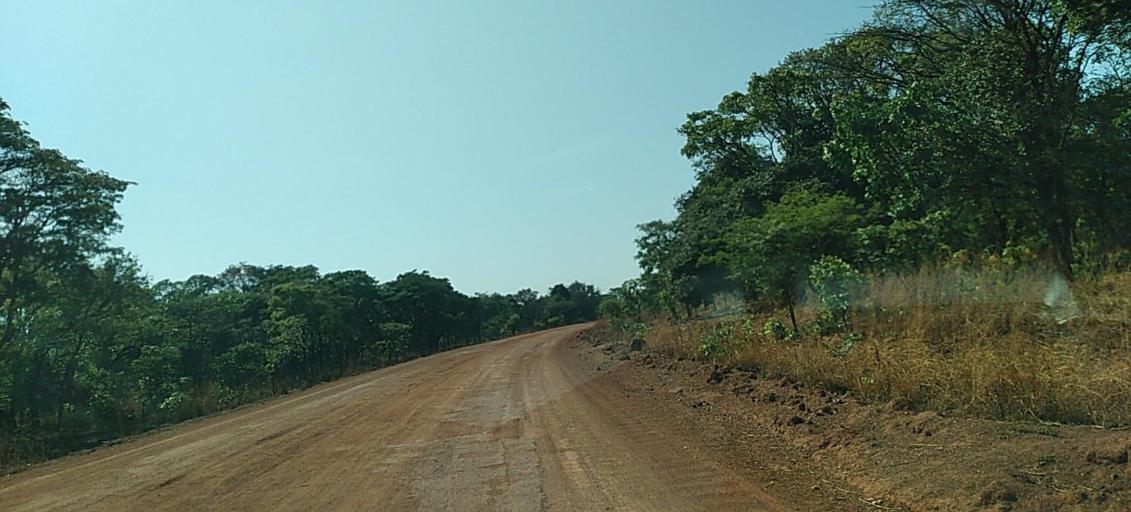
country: ZM
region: North-Western
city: Mwinilunga
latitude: -11.9203
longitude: 25.3160
